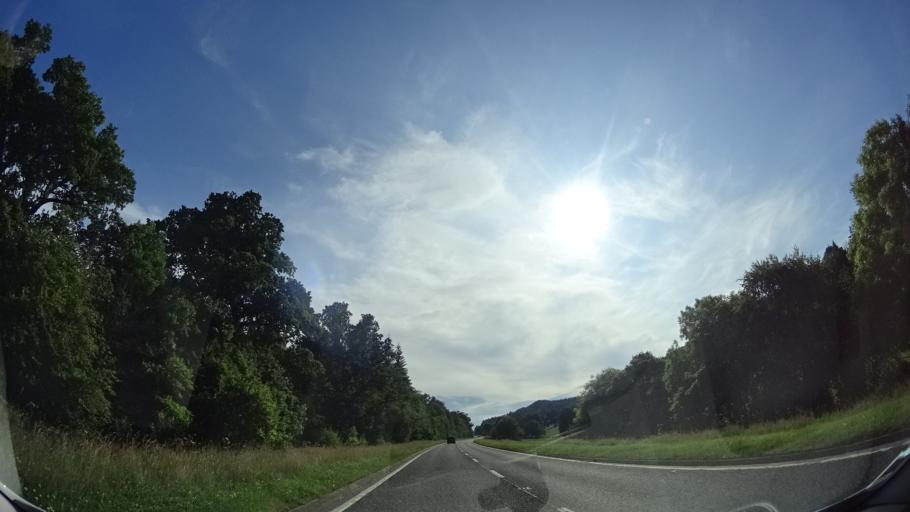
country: GB
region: Scotland
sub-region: Highland
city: Conon Bridge
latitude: 57.5725
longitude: -4.4550
